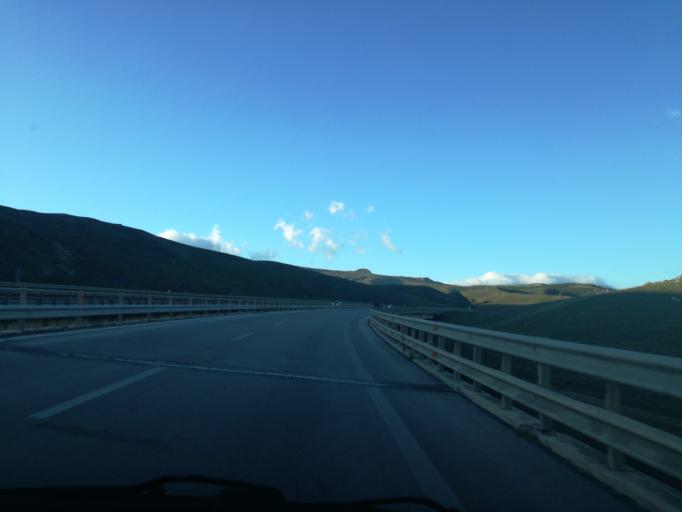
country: IT
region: Sicily
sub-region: Provincia di Caltanissetta
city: Resuttano
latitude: 37.7277
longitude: 14.0300
